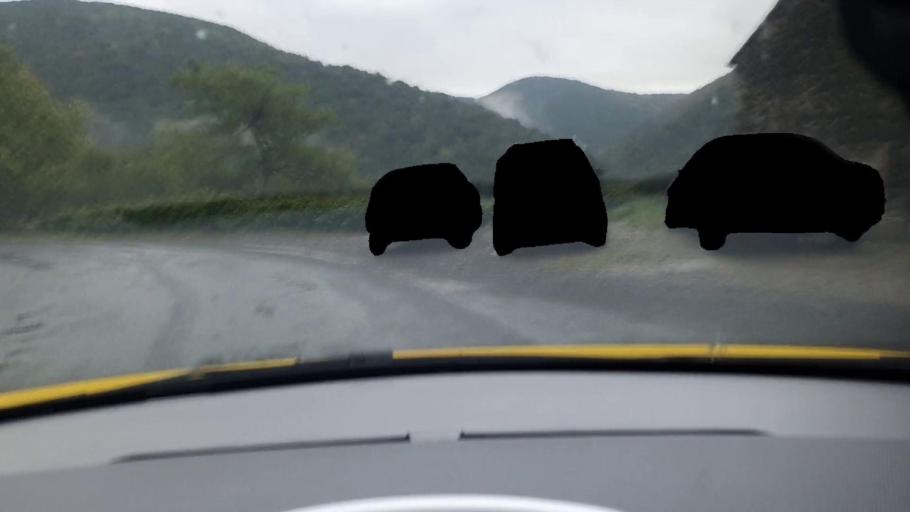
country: FR
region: Languedoc-Roussillon
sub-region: Departement du Gard
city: Sumene
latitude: 44.0010
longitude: 3.7129
